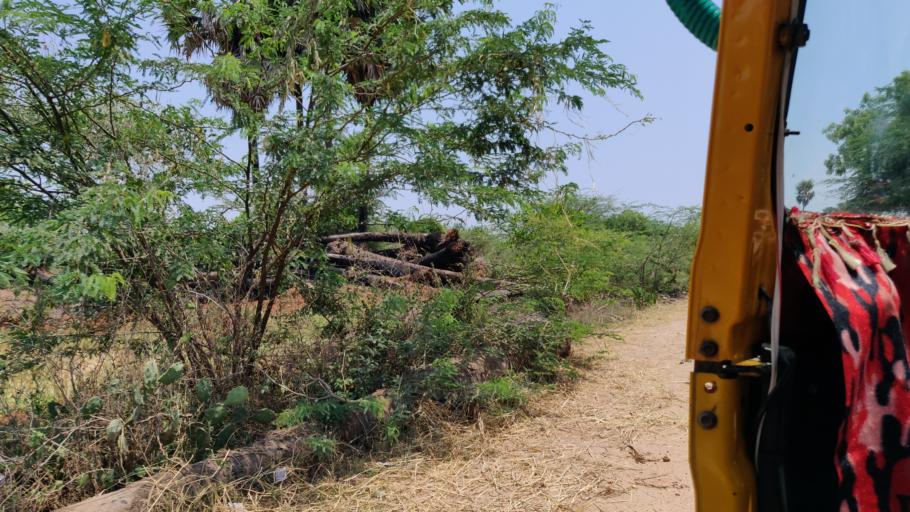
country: IN
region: Telangana
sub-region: Nalgonda
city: Mirialguda
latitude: 17.0129
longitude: 79.5462
